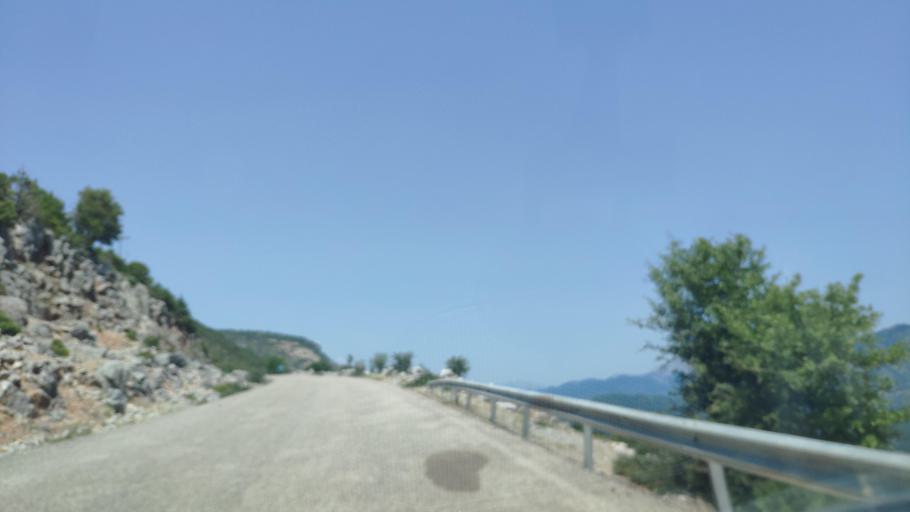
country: GR
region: Thessaly
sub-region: Nomos Kardhitsas
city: Anthiro
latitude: 39.1323
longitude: 21.3932
